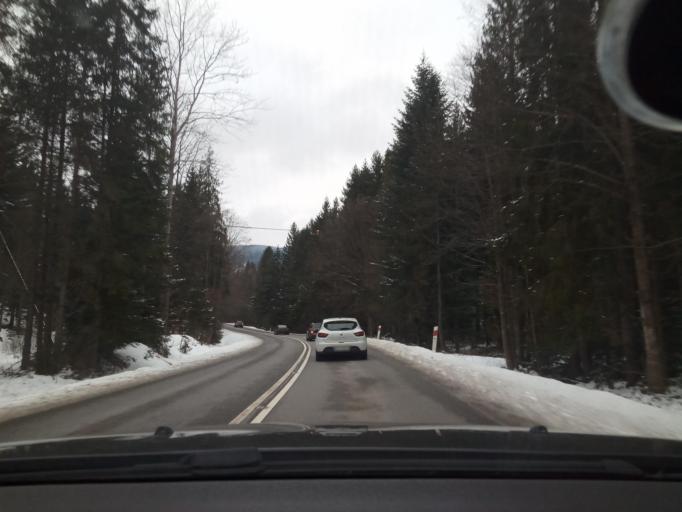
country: PL
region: Lesser Poland Voivodeship
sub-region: Powiat limanowski
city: Lubomierz
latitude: 49.6263
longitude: 20.2663
